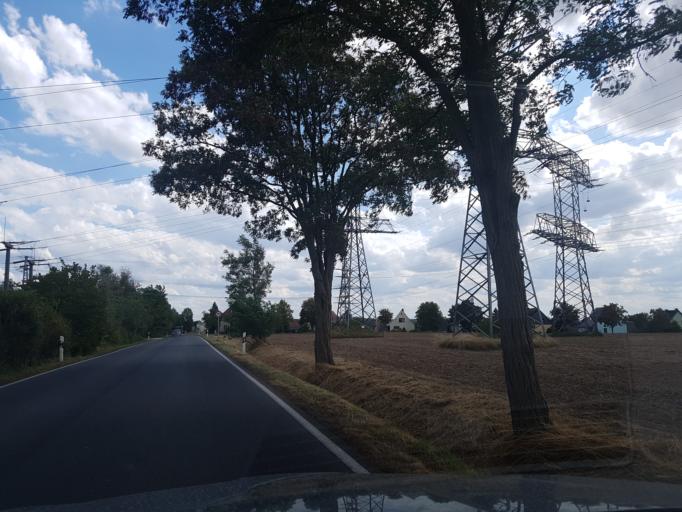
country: DE
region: Saxony
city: Priestewitz
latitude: 51.2362
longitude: 13.5450
